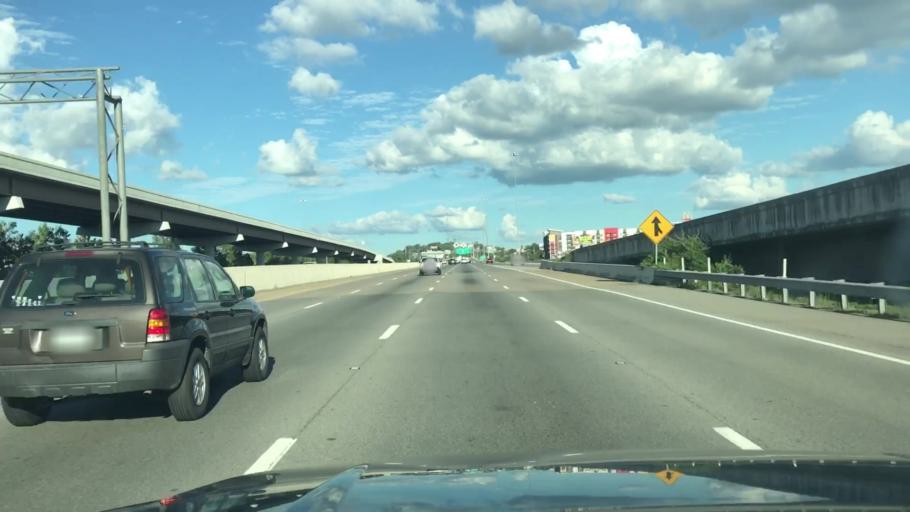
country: US
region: Tennessee
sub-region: Davidson County
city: Belle Meade
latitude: 36.1541
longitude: -86.8506
